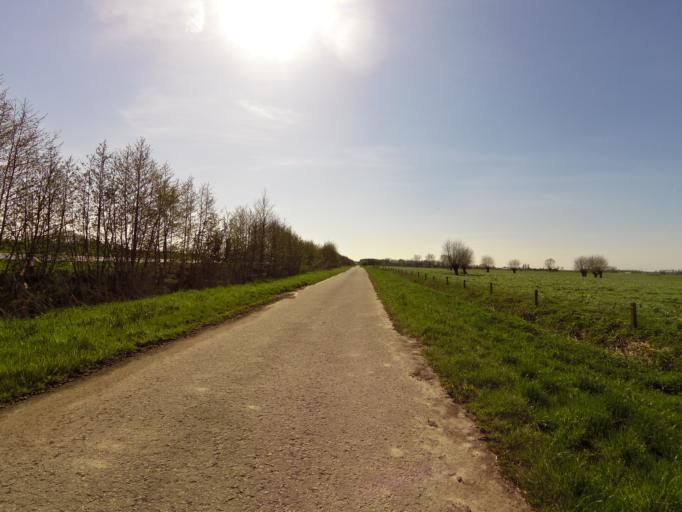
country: BE
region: Flanders
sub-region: Provincie West-Vlaanderen
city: Jabbeke
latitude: 51.1879
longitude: 3.0498
